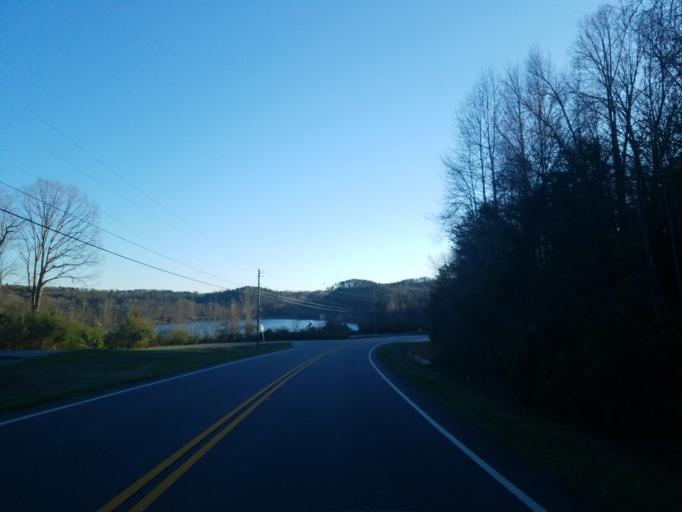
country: US
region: Georgia
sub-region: Lumpkin County
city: Dahlonega
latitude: 34.5528
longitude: -83.9690
